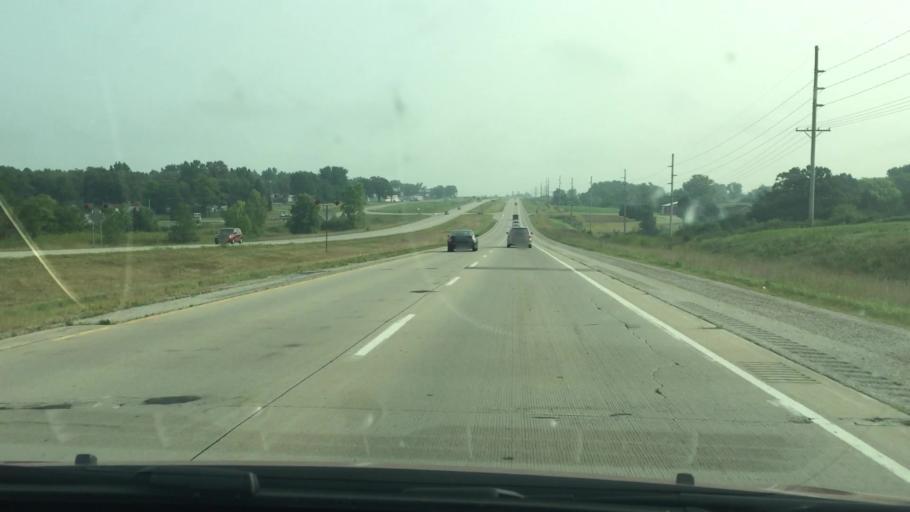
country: US
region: Iowa
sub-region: Muscatine County
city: Muscatine
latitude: 41.4676
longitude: -91.0041
